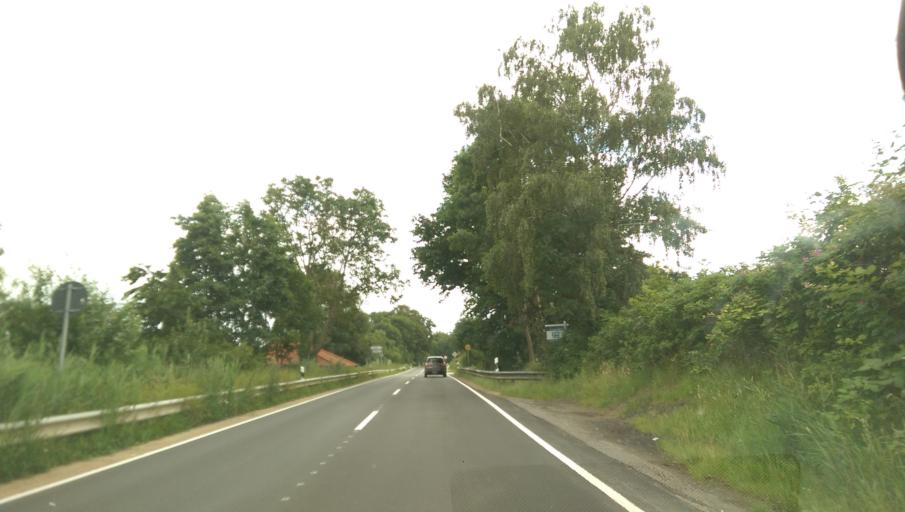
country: DE
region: Schleswig-Holstein
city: Timmendorfer Strand
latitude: 53.9910
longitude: 10.8241
